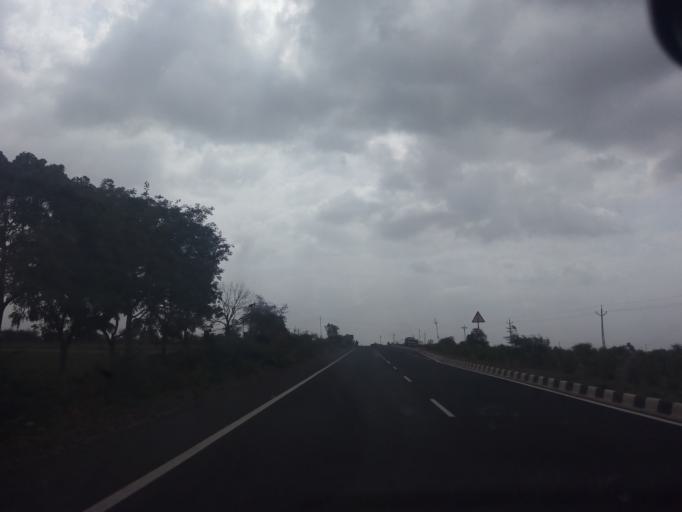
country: IN
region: Gujarat
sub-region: Surendranagar
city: Halvad
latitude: 23.0052
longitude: 71.1142
